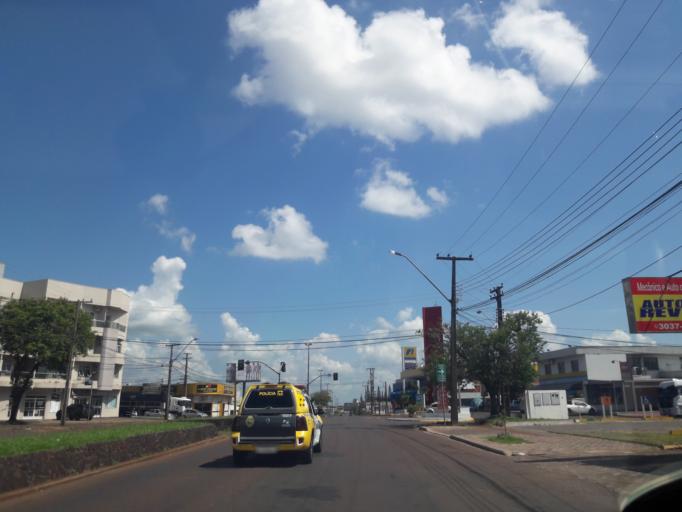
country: BR
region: Parana
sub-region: Cascavel
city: Cascavel
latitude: -24.9773
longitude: -53.4548
